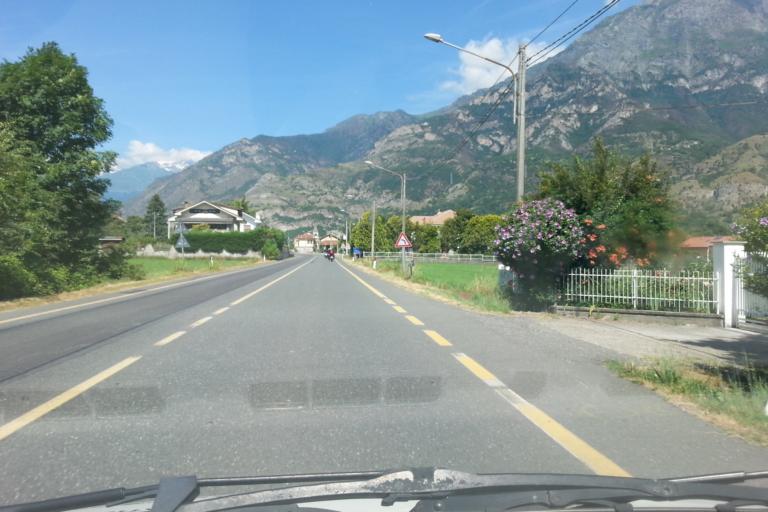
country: IT
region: Piedmont
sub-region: Provincia di Torino
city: Bussoleno
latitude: 45.1344
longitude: 7.1564
